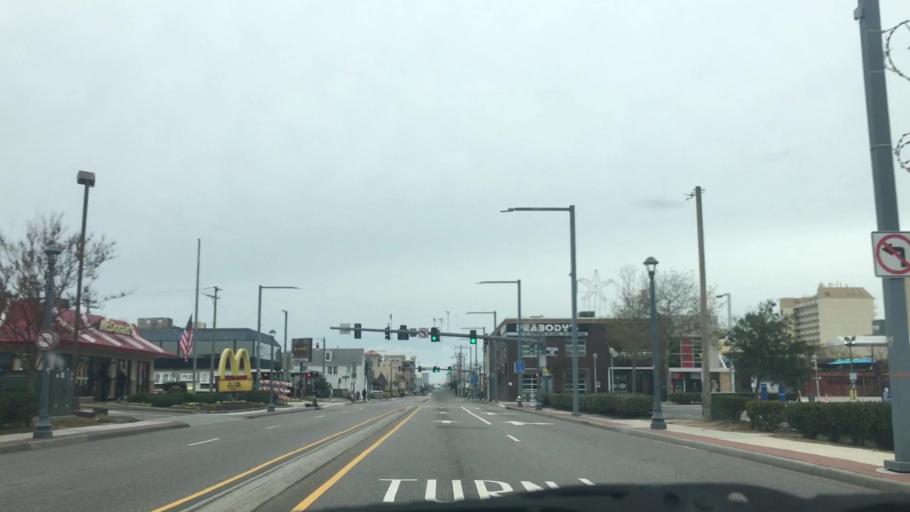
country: US
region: Virginia
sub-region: City of Virginia Beach
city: Virginia Beach
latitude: 36.8483
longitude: -75.9764
